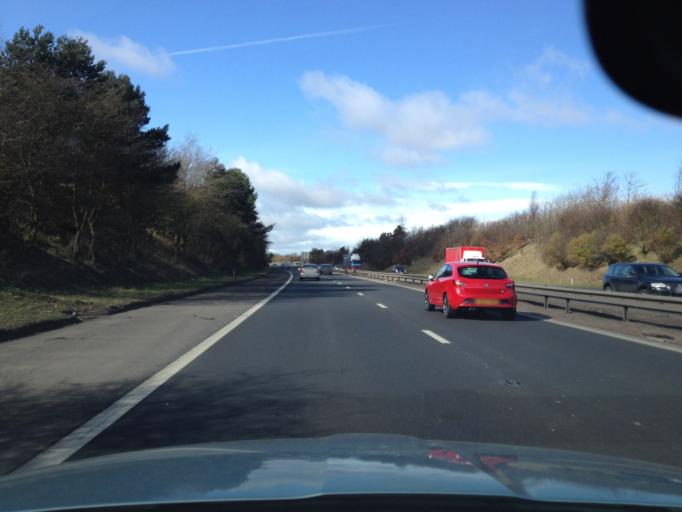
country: GB
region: Scotland
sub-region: Edinburgh
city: Newbridge
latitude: 55.9265
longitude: -3.4355
